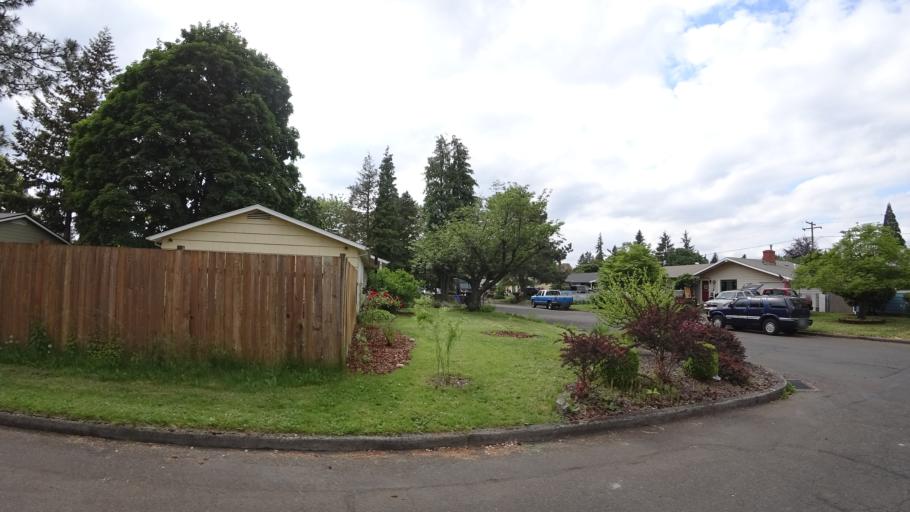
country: US
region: Oregon
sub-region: Multnomah County
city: Gresham
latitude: 45.5078
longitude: -122.4787
